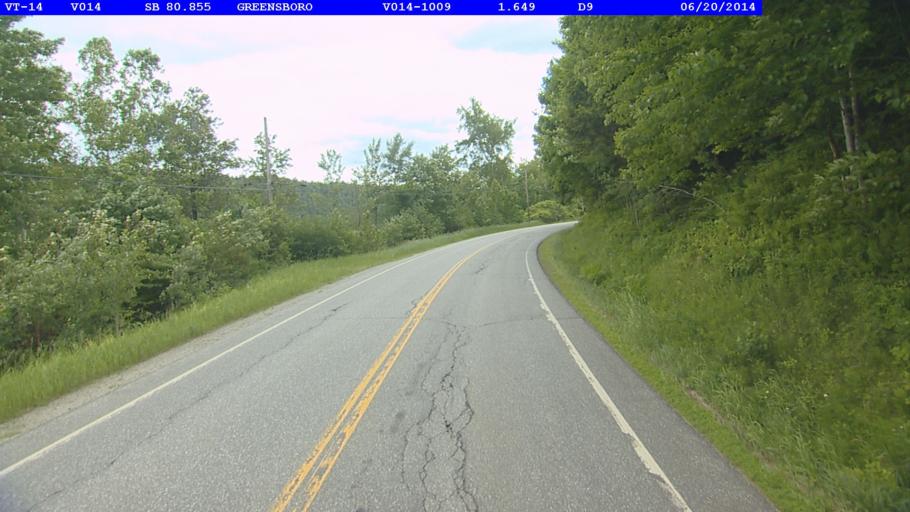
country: US
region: Vermont
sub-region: Caledonia County
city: Hardwick
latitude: 44.6026
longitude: -72.3583
